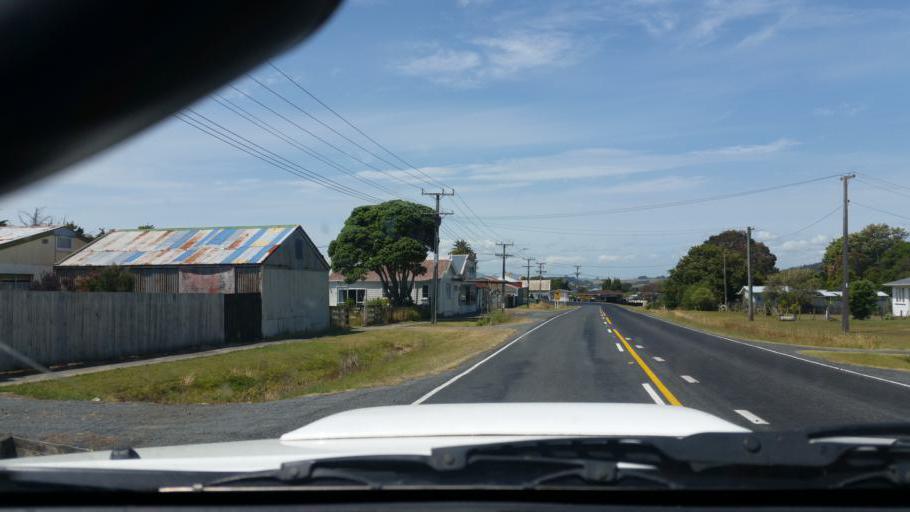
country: NZ
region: Northland
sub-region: Kaipara District
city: Dargaville
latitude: -36.0319
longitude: 173.9218
